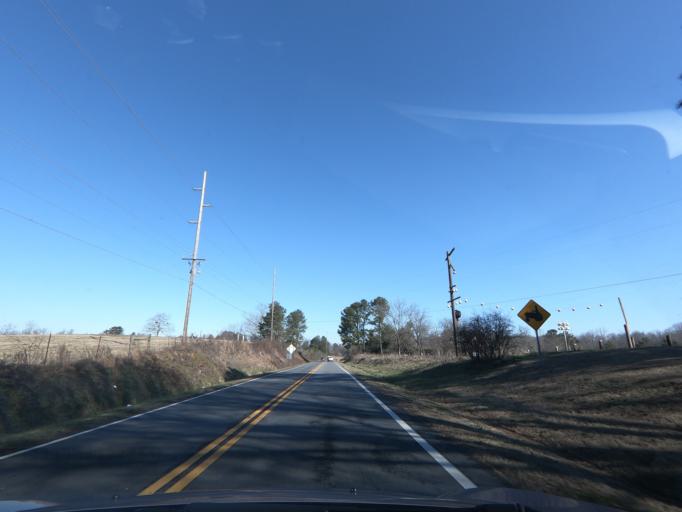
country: US
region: Georgia
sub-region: Forsyth County
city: Cumming
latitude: 34.3048
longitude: -84.1505
